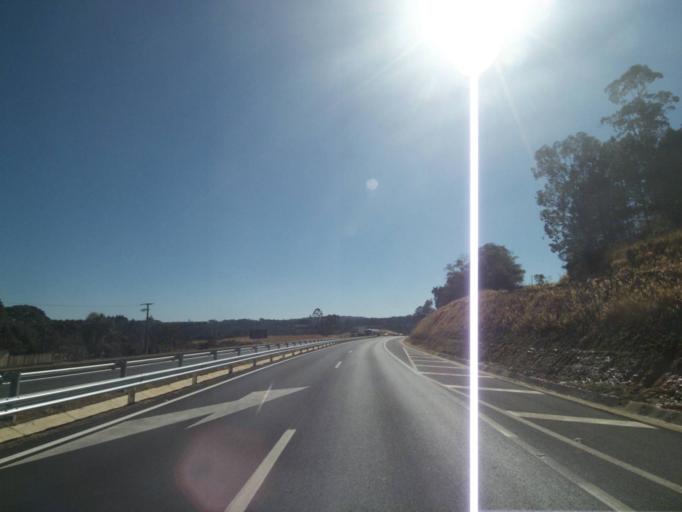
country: BR
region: Parana
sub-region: Tibagi
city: Tibagi
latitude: -24.7455
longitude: -50.5372
